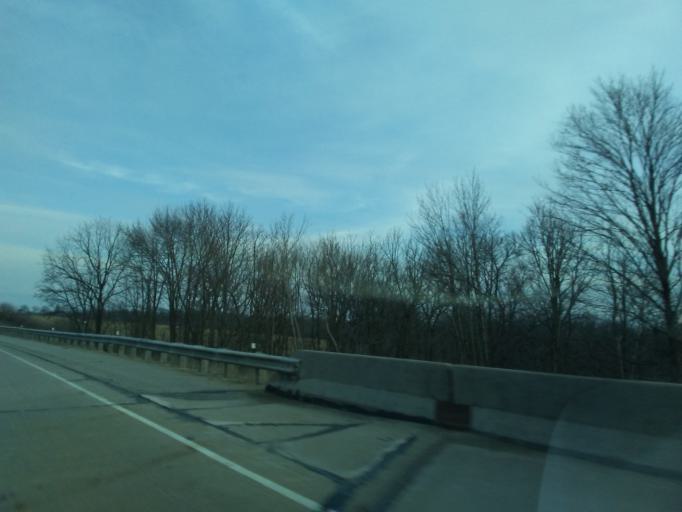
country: US
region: Wisconsin
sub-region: Dane County
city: Mount Horeb
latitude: 42.9938
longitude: -89.7450
